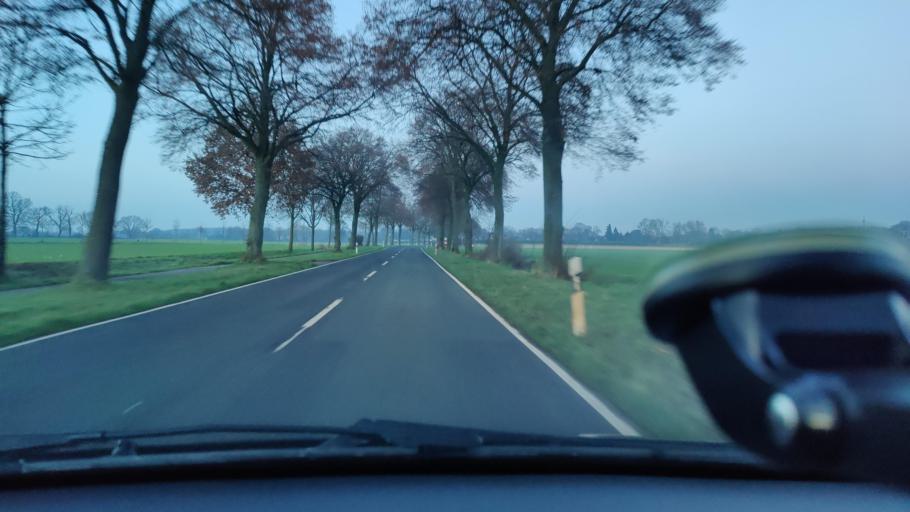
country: DE
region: North Rhine-Westphalia
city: Rheinberg
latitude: 51.6018
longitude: 6.6111
